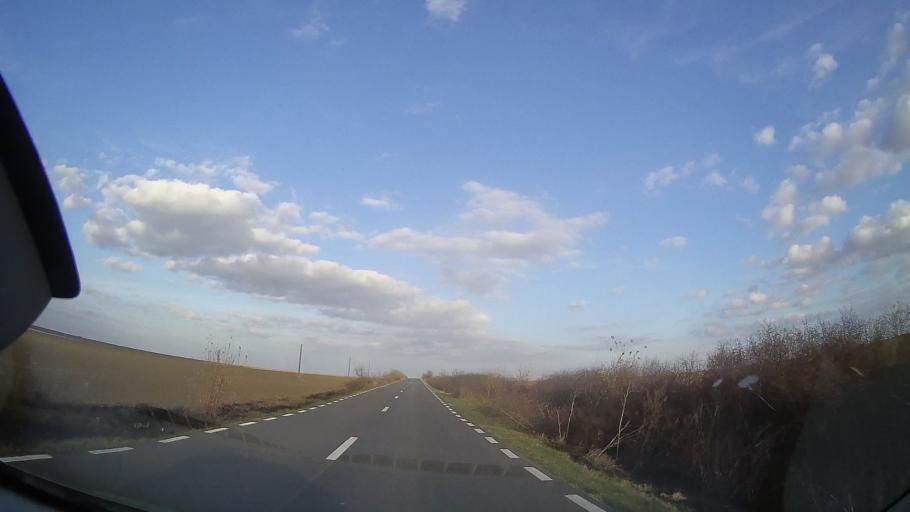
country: RO
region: Constanta
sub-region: Comuna Dumbraveni
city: Dumbraveni
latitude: 43.9348
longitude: 28.0276
